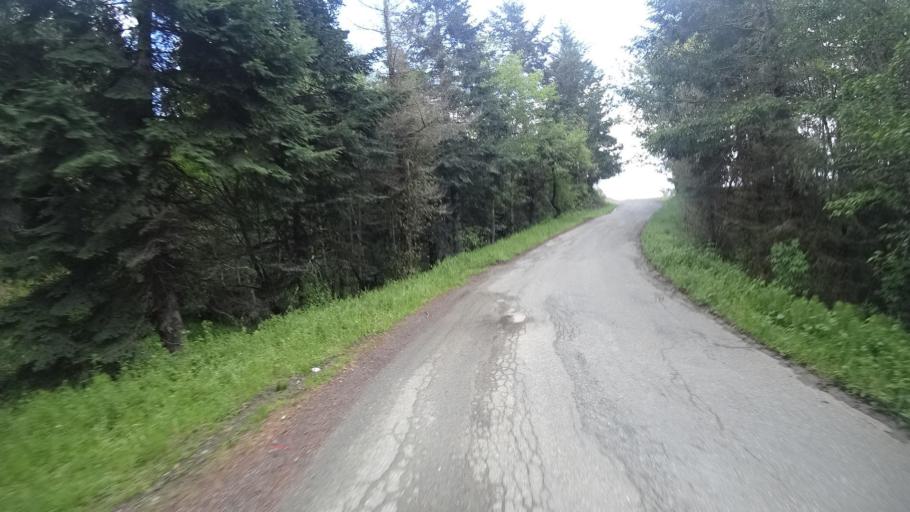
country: US
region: California
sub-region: Humboldt County
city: Blue Lake
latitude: 40.8572
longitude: -123.9272
